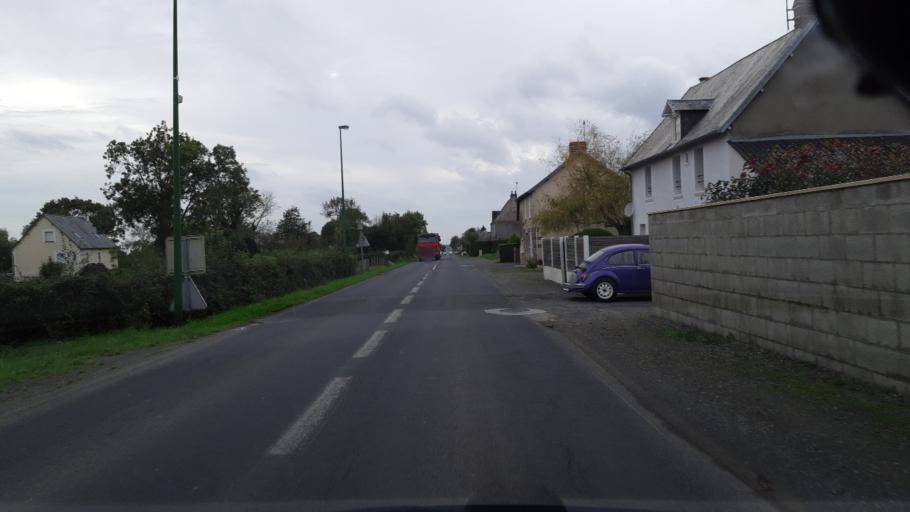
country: FR
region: Lower Normandy
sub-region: Departement de la Manche
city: Gavray
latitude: 48.9328
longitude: -1.3848
